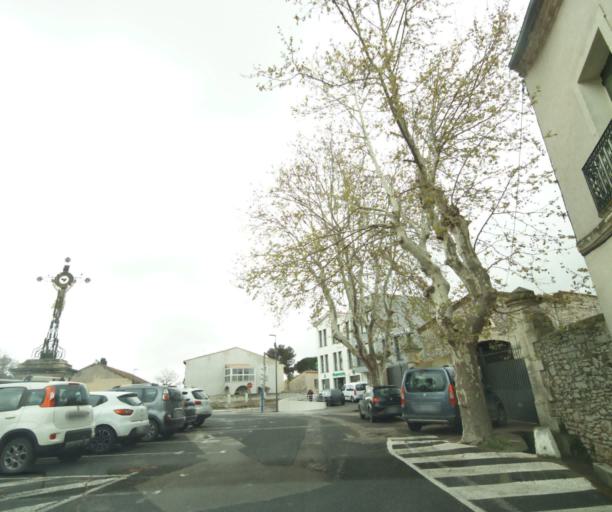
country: FR
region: Languedoc-Roussillon
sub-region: Departement de l'Herault
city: Cournonterral
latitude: 43.5556
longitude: 3.7216
